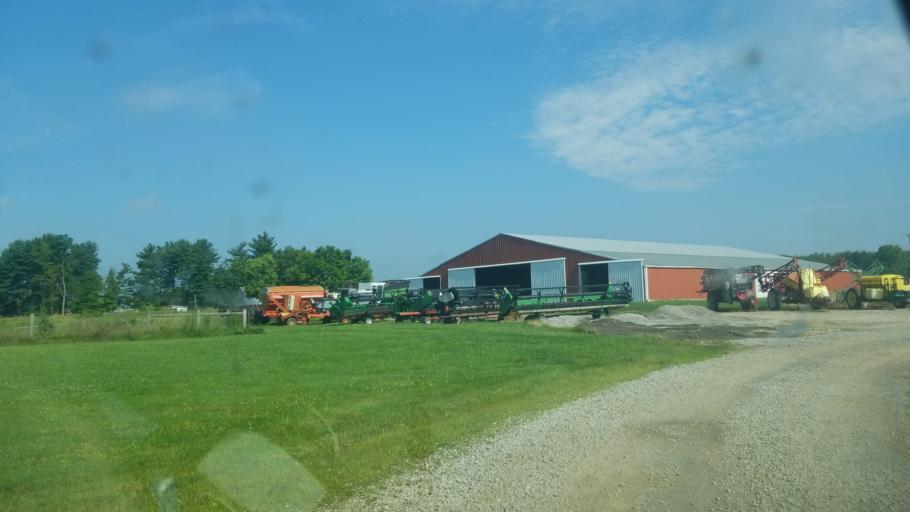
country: US
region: Ohio
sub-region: Knox County
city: Fredericktown
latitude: 40.5332
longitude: -82.5102
